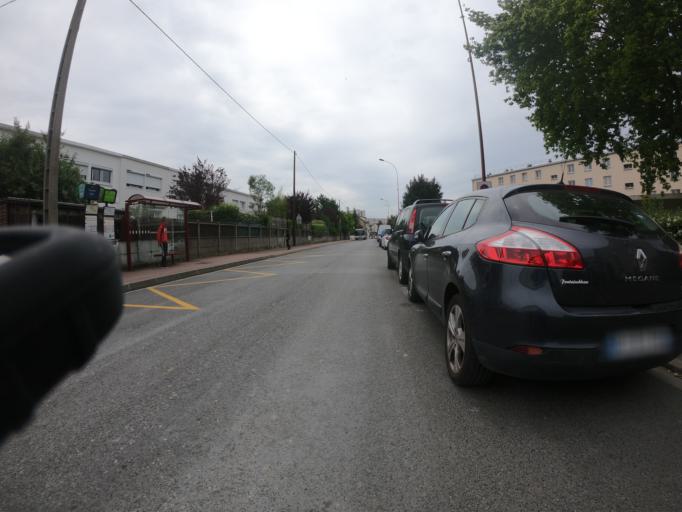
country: FR
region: Ile-de-France
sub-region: Departement du Val-de-Marne
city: Fresnes
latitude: 48.7614
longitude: 2.3264
